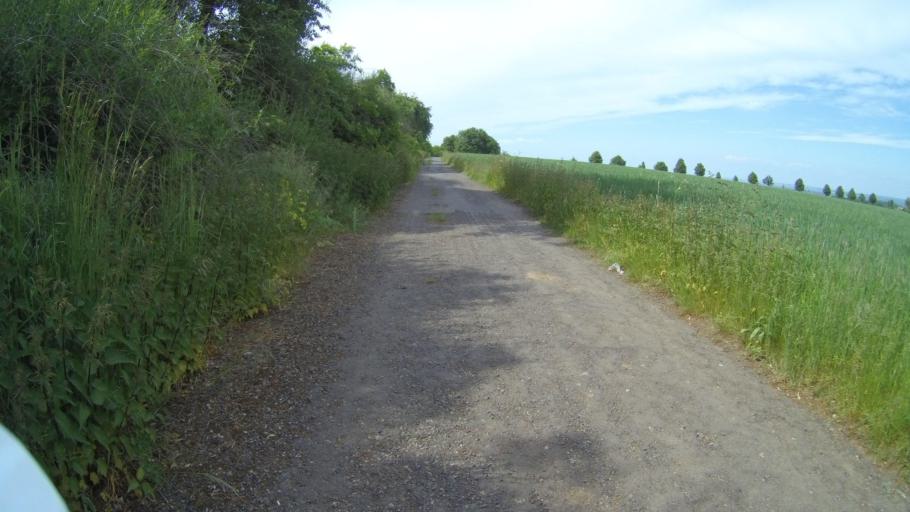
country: CZ
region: Central Bohemia
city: Libeznice
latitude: 50.1914
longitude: 14.4698
